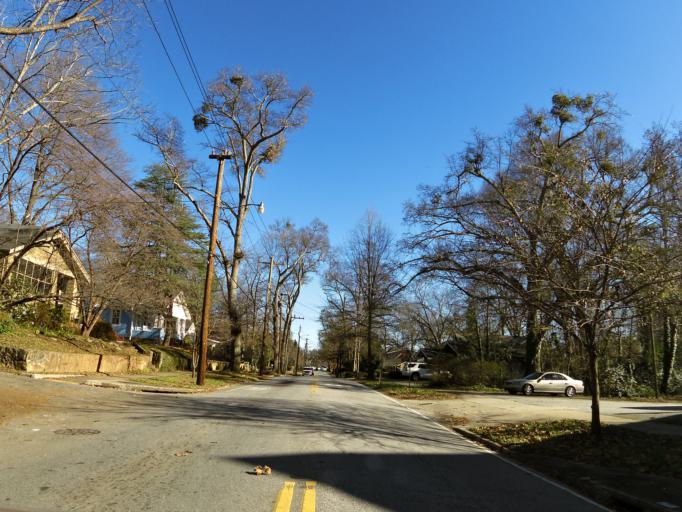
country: US
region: South Carolina
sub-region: Greenville County
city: Greenville
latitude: 34.8592
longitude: -82.4001
